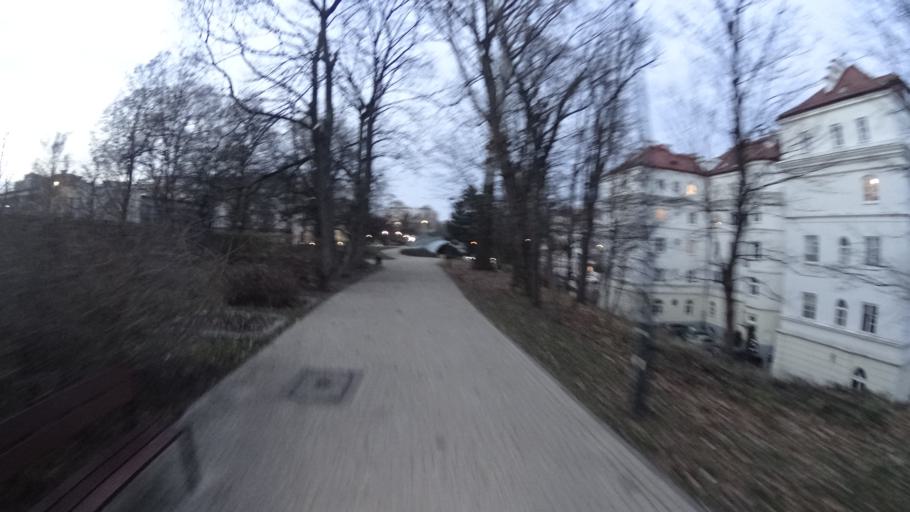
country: PL
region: Masovian Voivodeship
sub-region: Warszawa
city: Srodmiescie
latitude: 52.2233
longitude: 21.0306
